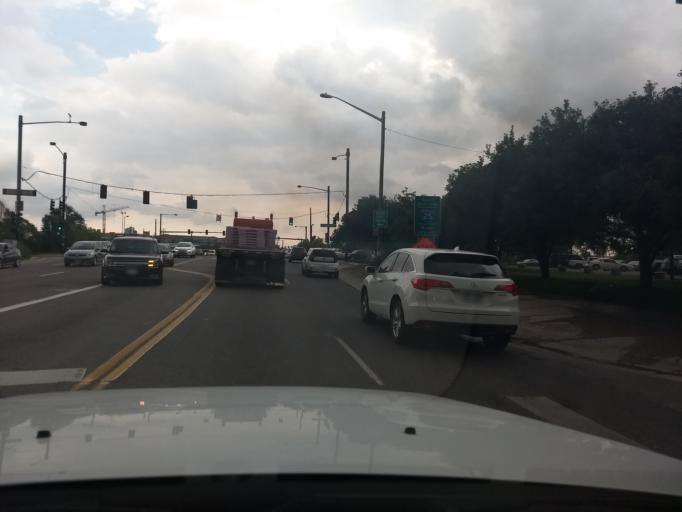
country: US
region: Colorado
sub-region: Denver County
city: Denver
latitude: 39.7111
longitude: -105.0015
